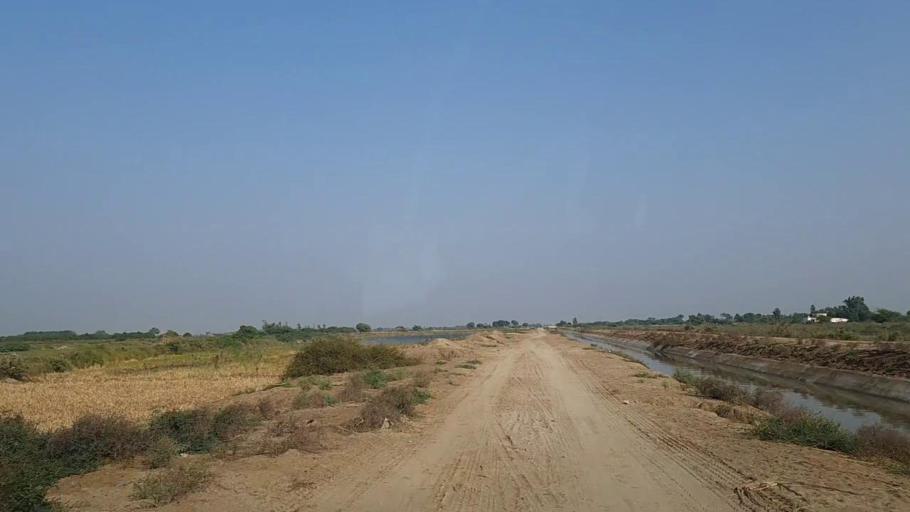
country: PK
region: Sindh
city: Mirpur Sakro
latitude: 24.6154
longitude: 67.7134
